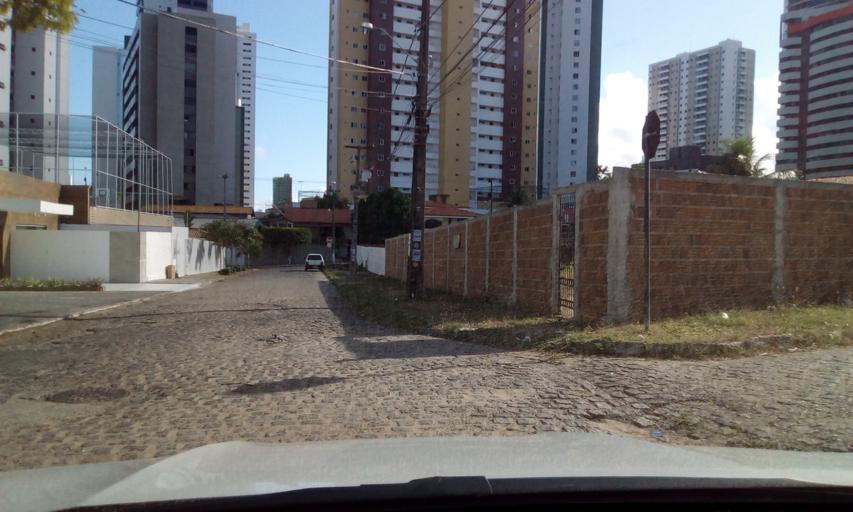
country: BR
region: Paraiba
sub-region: Joao Pessoa
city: Joao Pessoa
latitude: -7.1145
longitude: -34.8375
